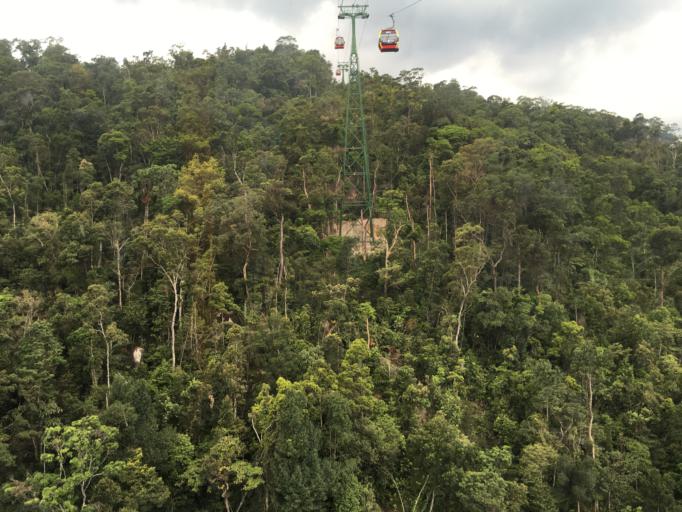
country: VN
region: Da Nang
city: Hoa Vang
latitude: 16.0167
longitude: 108.0160
